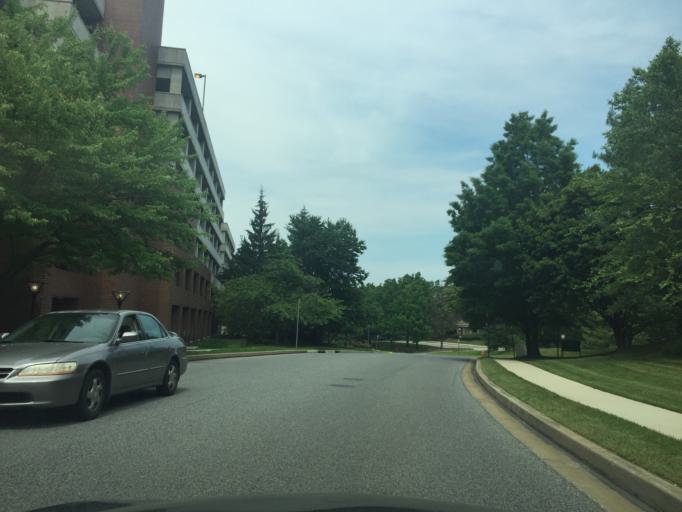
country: US
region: Maryland
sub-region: Baltimore County
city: Towson
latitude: 39.4066
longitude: -76.5986
